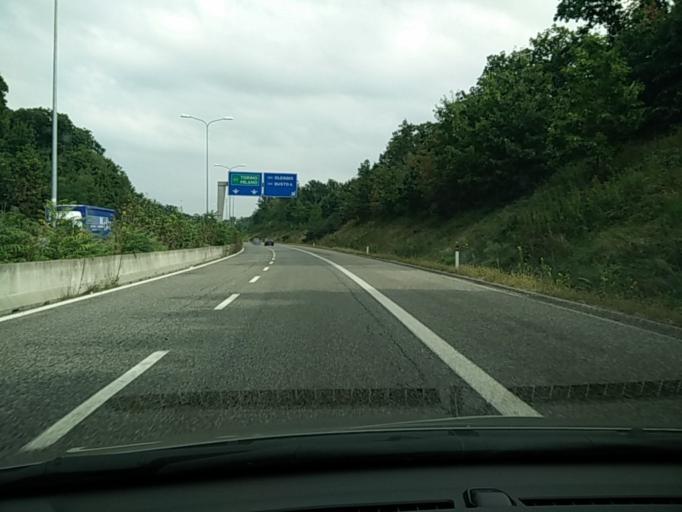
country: IT
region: Lombardy
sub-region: Provincia di Varese
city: Lonate Pozzolo
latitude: 45.5859
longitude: 8.7194
